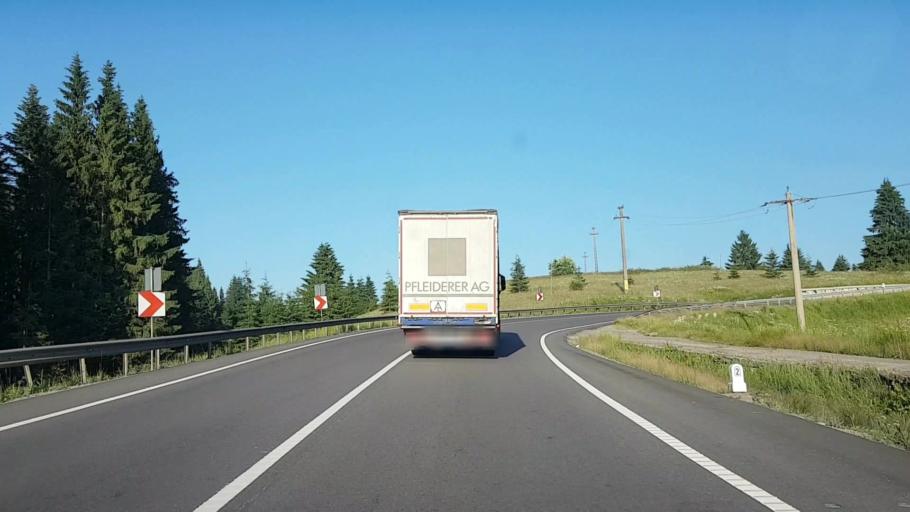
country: RO
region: Suceava
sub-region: Comuna Poiana Stampei
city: Poiana Stampei
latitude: 47.2869
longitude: 25.0661
